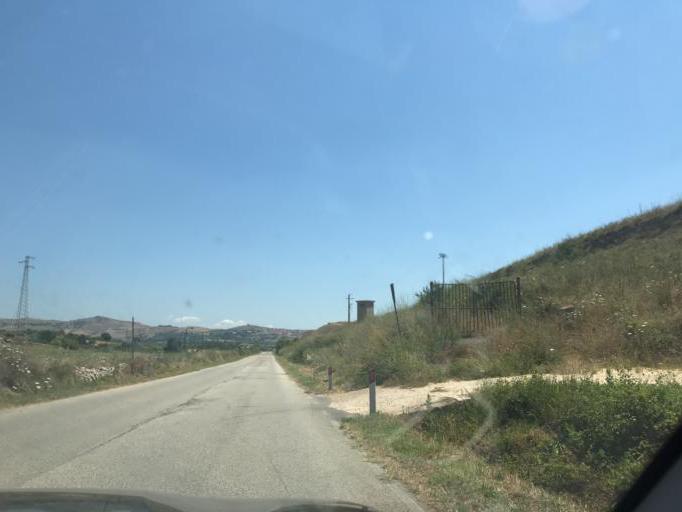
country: IT
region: Sardinia
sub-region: Provincia di Sassari
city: Codrongianos
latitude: 40.6506
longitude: 8.6919
